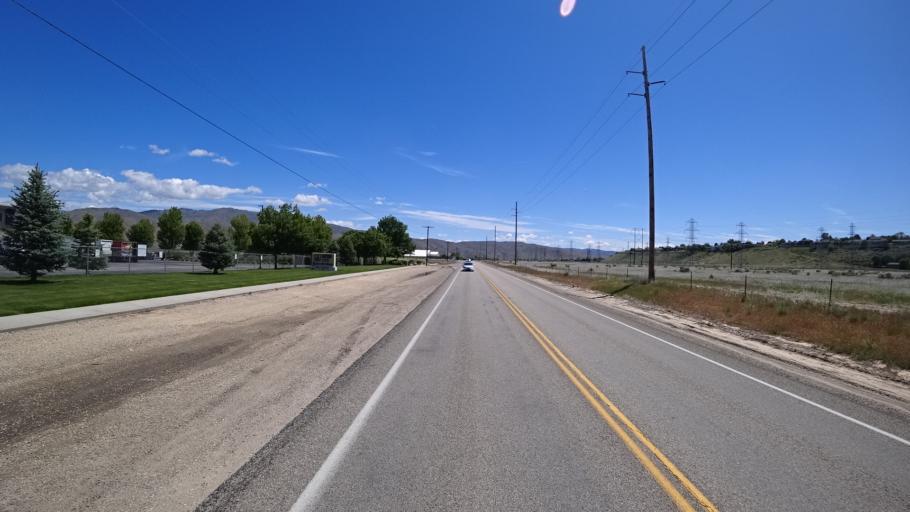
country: US
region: Idaho
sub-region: Ada County
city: Boise
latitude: 43.5605
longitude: -116.1477
